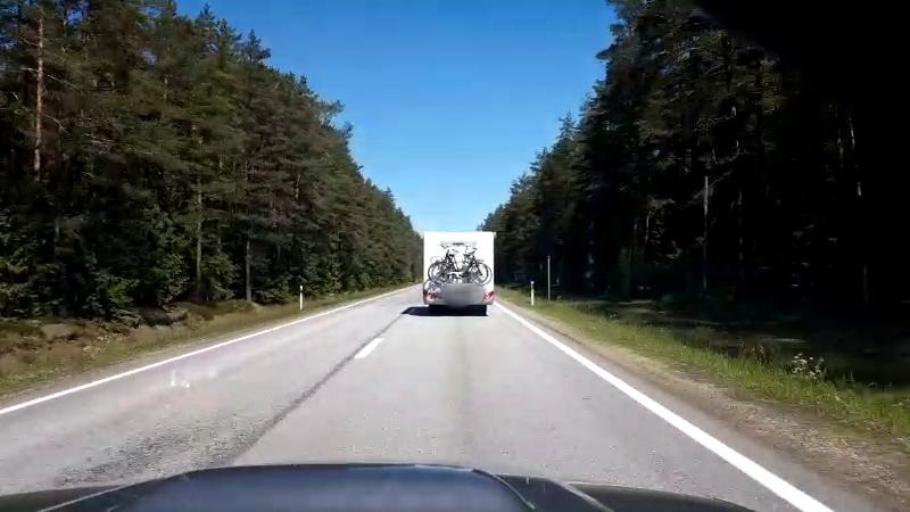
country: LV
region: Salacgrivas
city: Salacgriva
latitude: 57.5378
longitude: 24.4315
